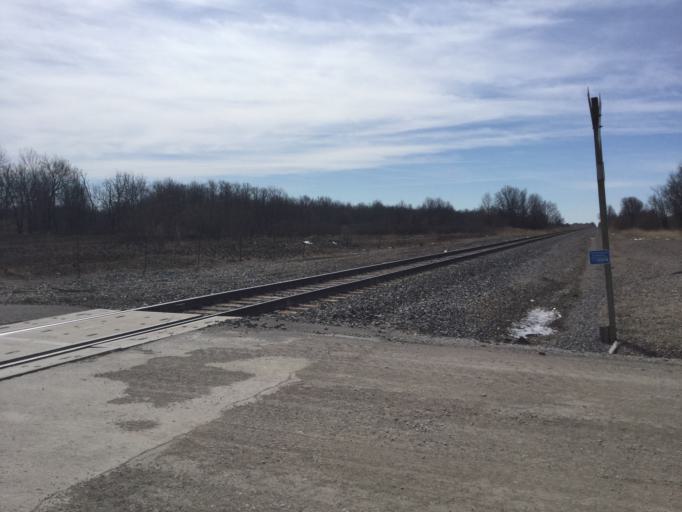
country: US
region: Kansas
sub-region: Cherokee County
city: Columbus
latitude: 37.2519
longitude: -94.8265
